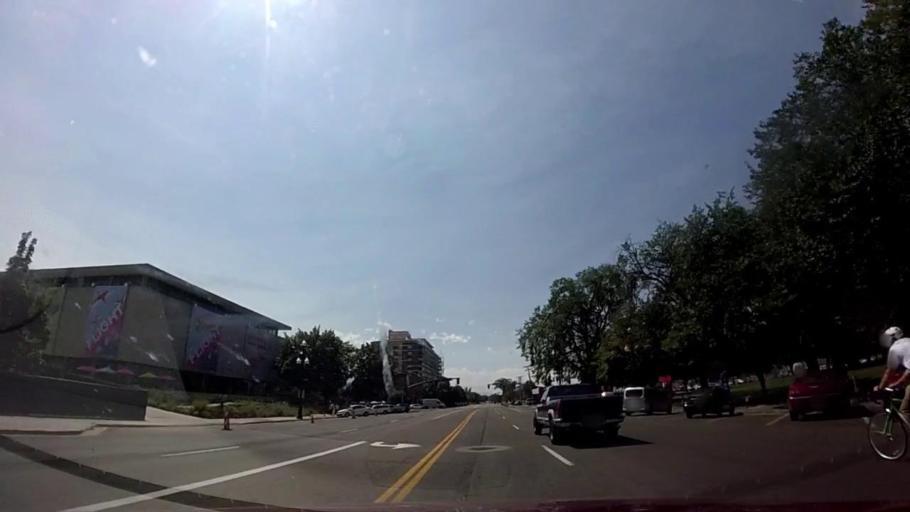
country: US
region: Utah
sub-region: Salt Lake County
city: Salt Lake City
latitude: 40.7593
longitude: -111.8854
